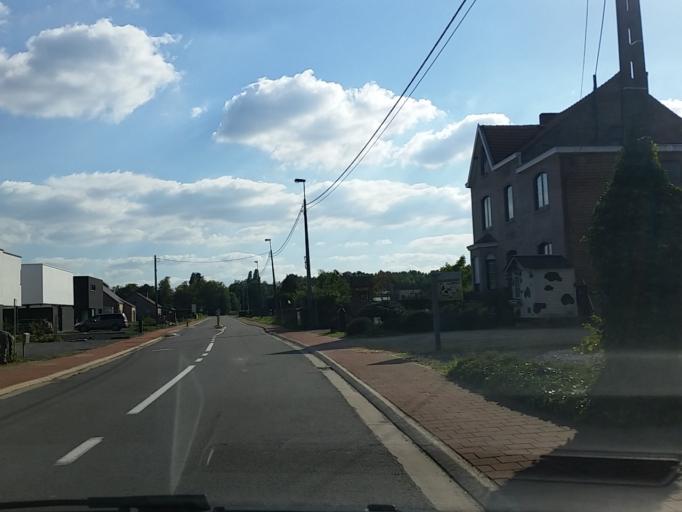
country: BE
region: Flanders
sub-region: Provincie Vlaams-Brabant
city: Haacht
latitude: 50.9342
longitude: 4.6164
